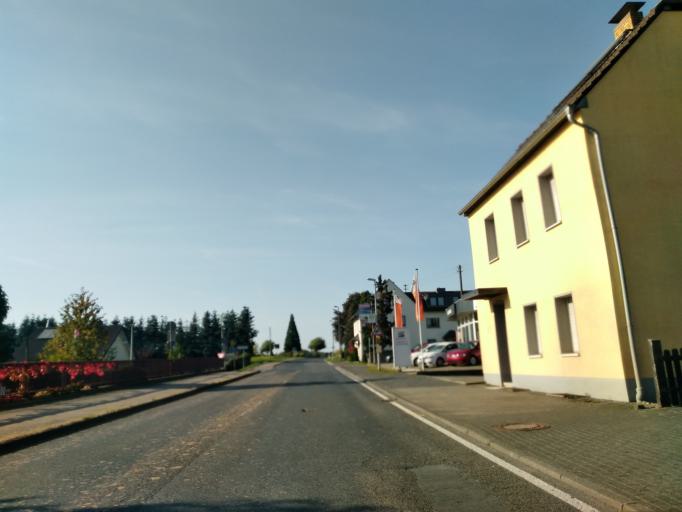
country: DE
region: North Rhine-Westphalia
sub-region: Regierungsbezirk Koln
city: Hennef
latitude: 50.7340
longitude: 7.2590
